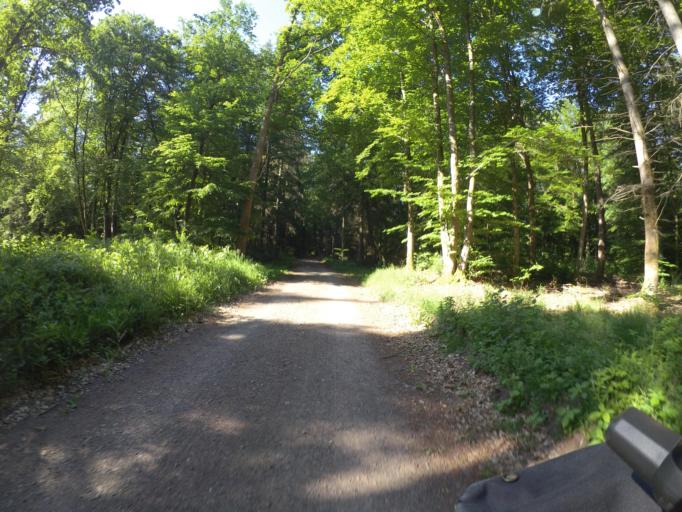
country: DE
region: Rheinland-Pfalz
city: Schonenberg-Kubelberg
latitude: 49.3810
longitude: 7.3635
